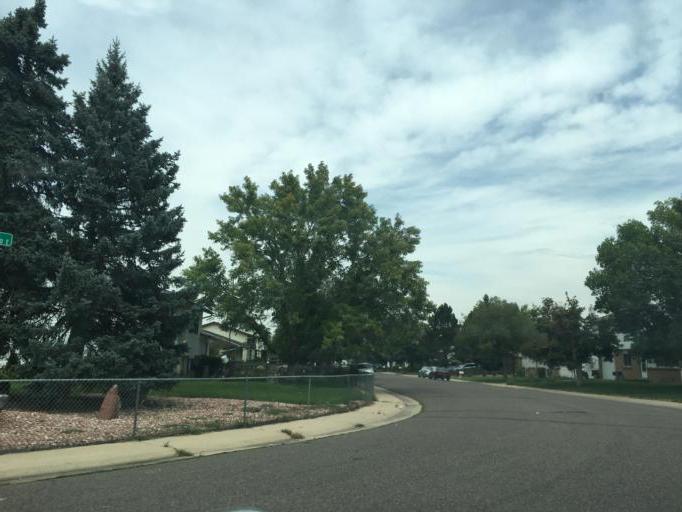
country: US
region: Colorado
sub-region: Adams County
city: Aurora
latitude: 39.7333
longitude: -104.7943
